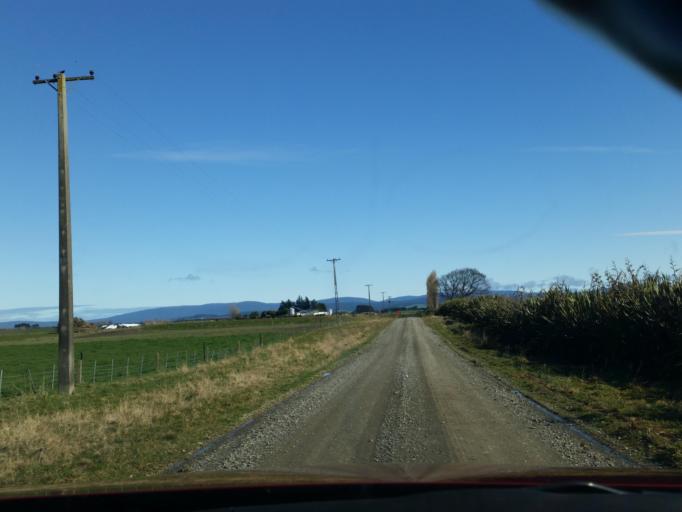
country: NZ
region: Southland
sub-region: Southland District
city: Winton
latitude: -46.1882
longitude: 168.1610
